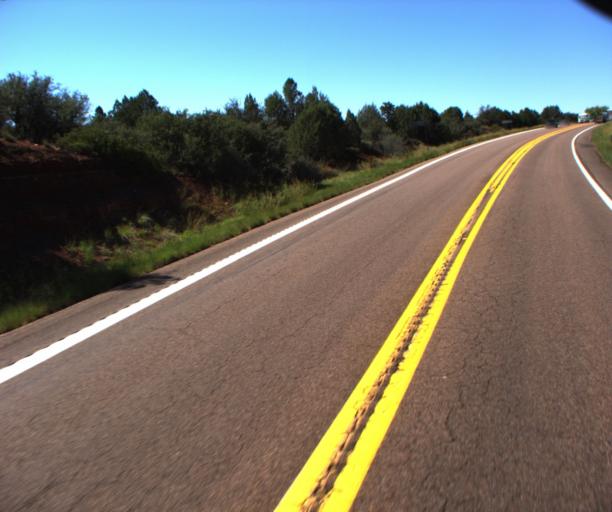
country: US
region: Arizona
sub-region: Navajo County
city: Cibecue
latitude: 34.0069
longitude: -110.2531
